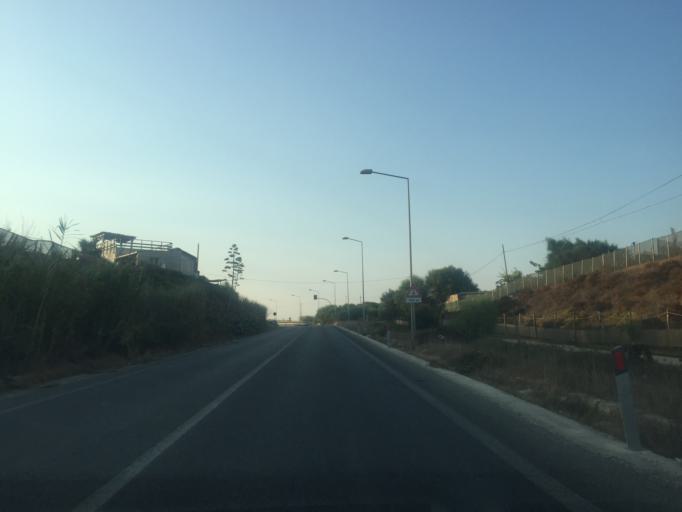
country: IT
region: Sicily
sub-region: Ragusa
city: Cava d'Aliga
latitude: 36.7162
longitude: 14.7578
